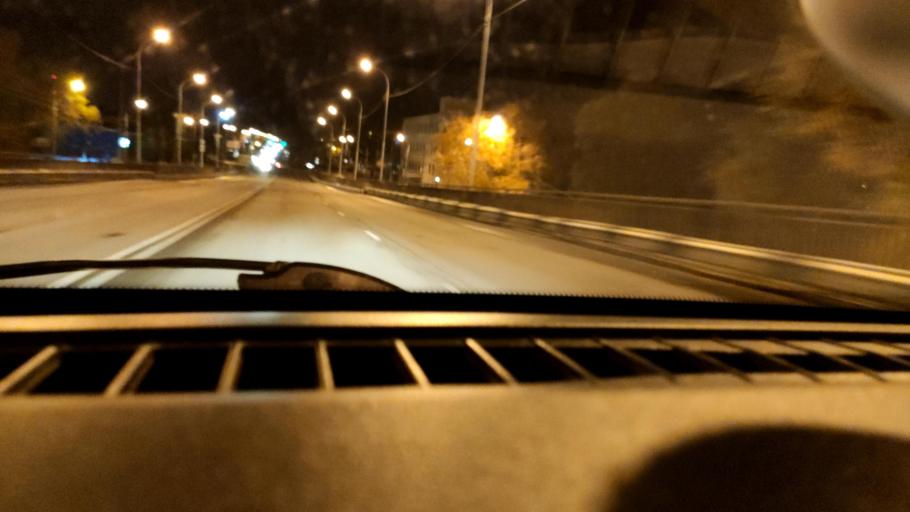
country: RU
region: Samara
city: Smyshlyayevka
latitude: 53.2261
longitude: 50.2858
